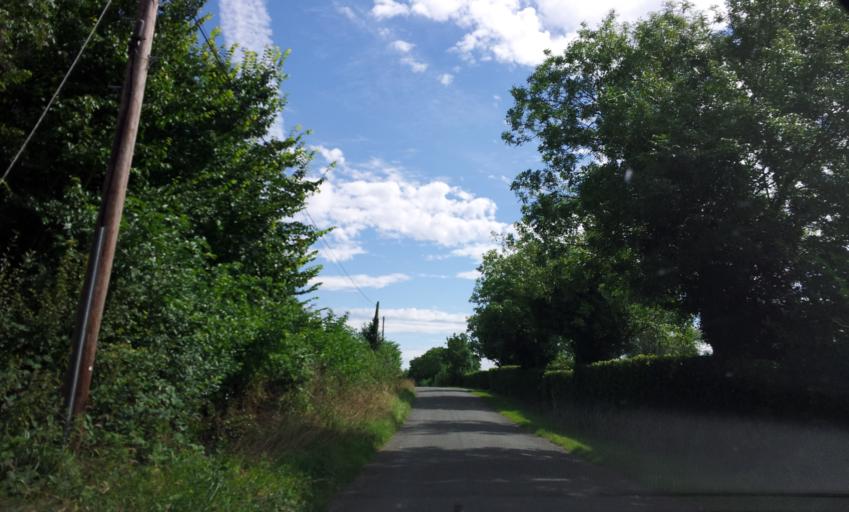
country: IE
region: Leinster
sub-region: Kildare
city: Moone
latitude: 52.9866
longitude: -6.8440
